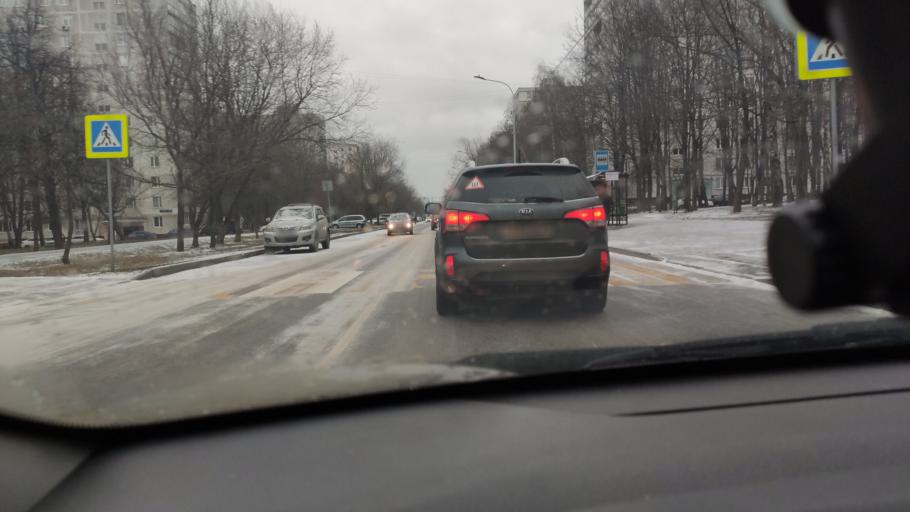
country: RU
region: Moscow
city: Chertanovo Yuzhnoye
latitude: 55.6020
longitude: 37.6150
